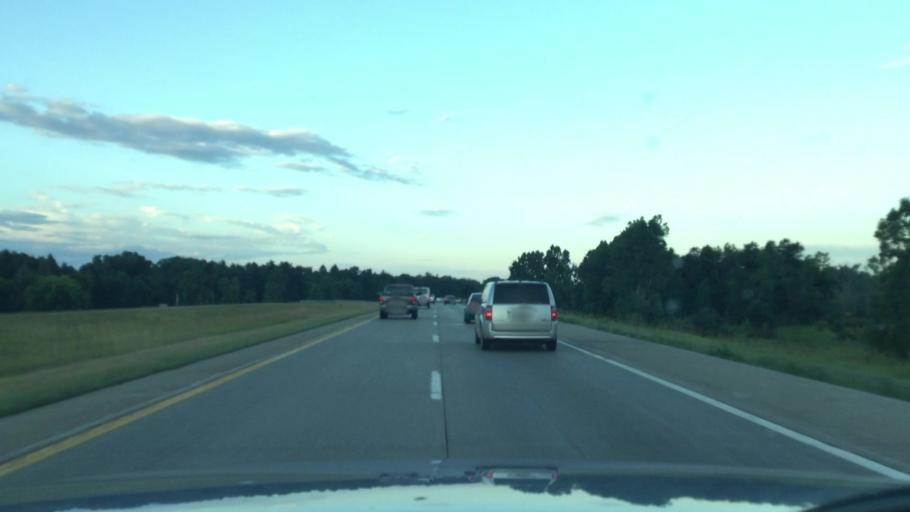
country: US
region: Michigan
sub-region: Shiawassee County
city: Perry
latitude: 42.8226
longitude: -84.2685
